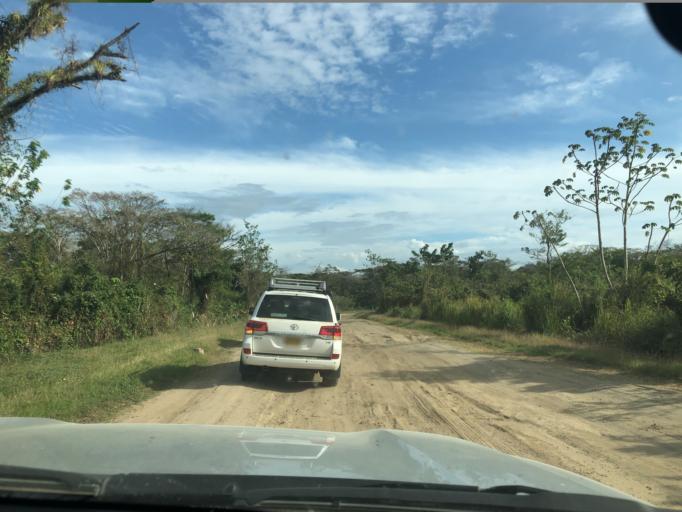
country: CR
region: Alajuela
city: San Jose
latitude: 11.1168
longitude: -85.2837
